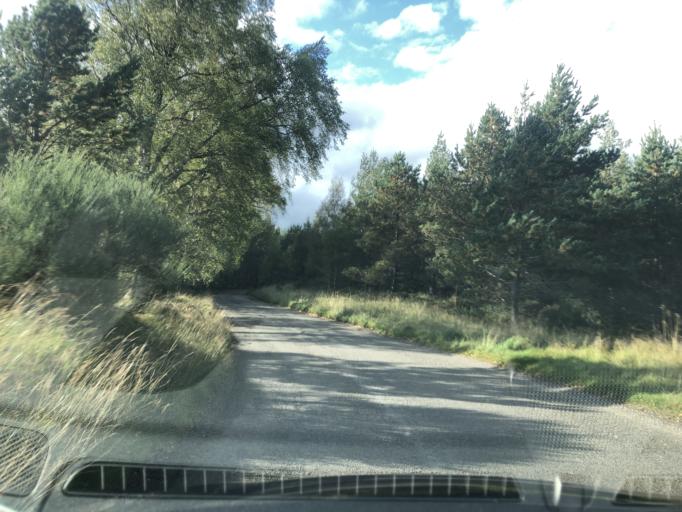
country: GB
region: Scotland
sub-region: Highland
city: Aviemore
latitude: 57.1124
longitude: -3.8899
